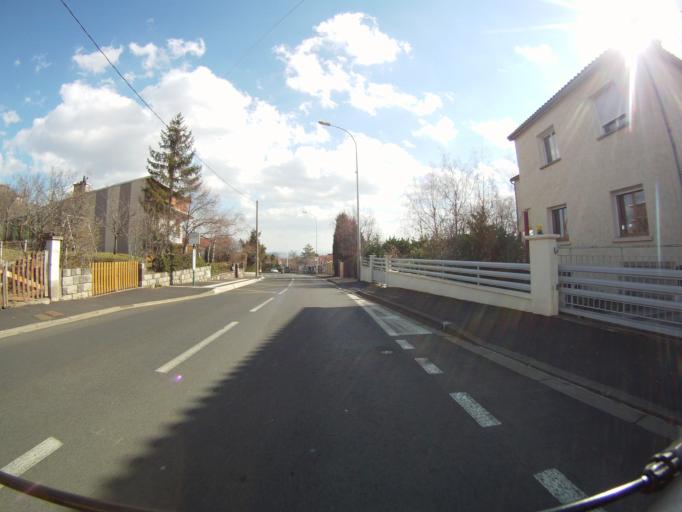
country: FR
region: Auvergne
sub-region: Departement du Puy-de-Dome
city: Beaumont
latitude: 45.7509
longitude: 3.0767
